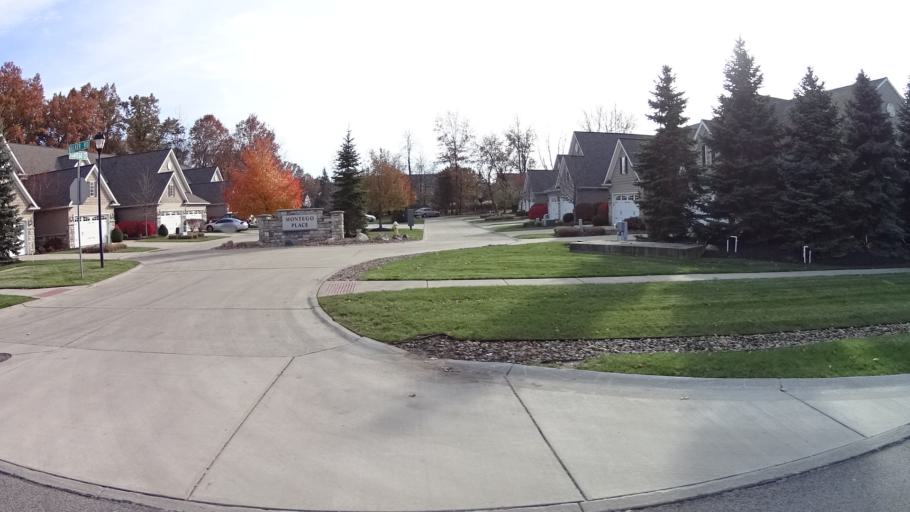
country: US
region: Ohio
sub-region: Lorain County
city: Avon Lake
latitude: 41.4928
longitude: -81.9879
